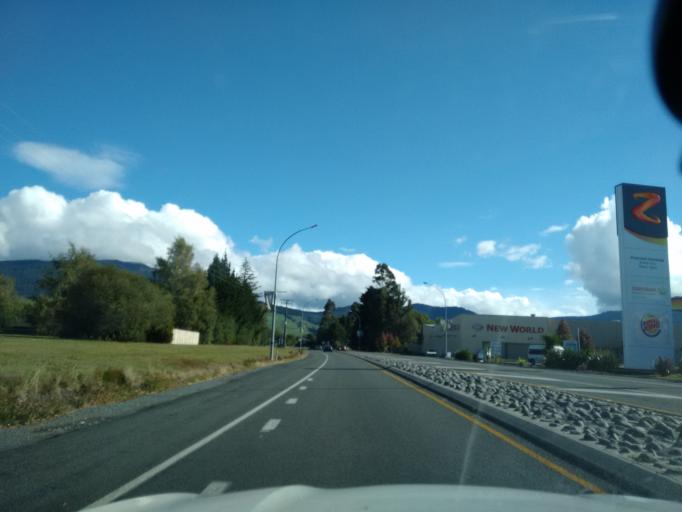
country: NZ
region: Waikato
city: Turangi
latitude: -38.9908
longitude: 175.8105
